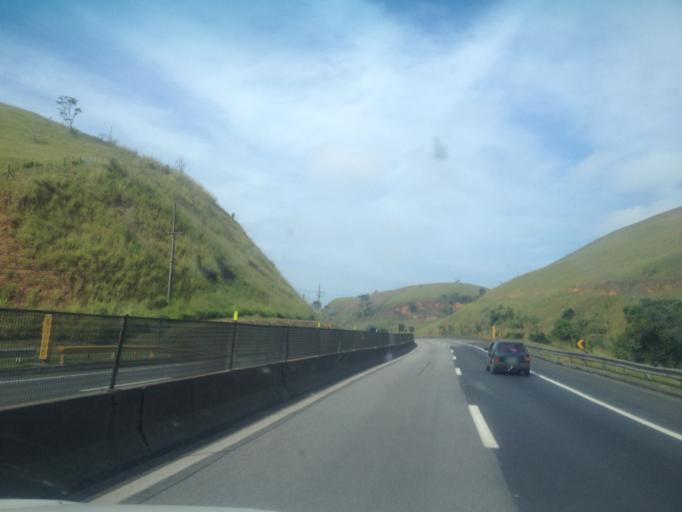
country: BR
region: Rio de Janeiro
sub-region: Pirai
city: Pirai
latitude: -22.6396
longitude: -43.8987
